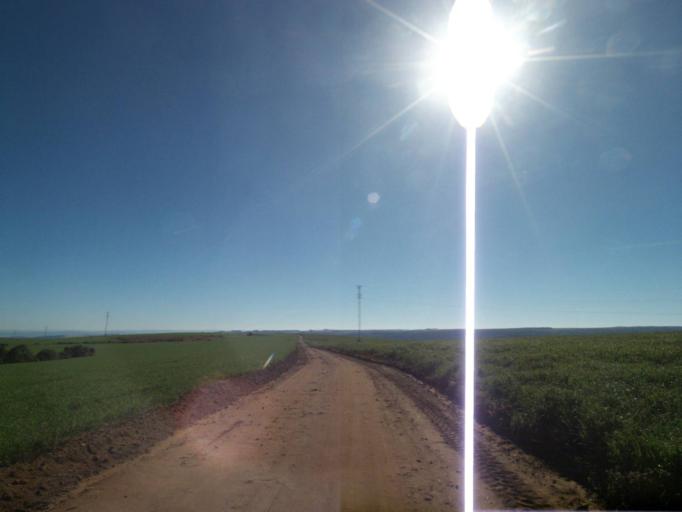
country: BR
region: Parana
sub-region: Tibagi
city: Tibagi
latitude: -24.5807
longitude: -50.2658
